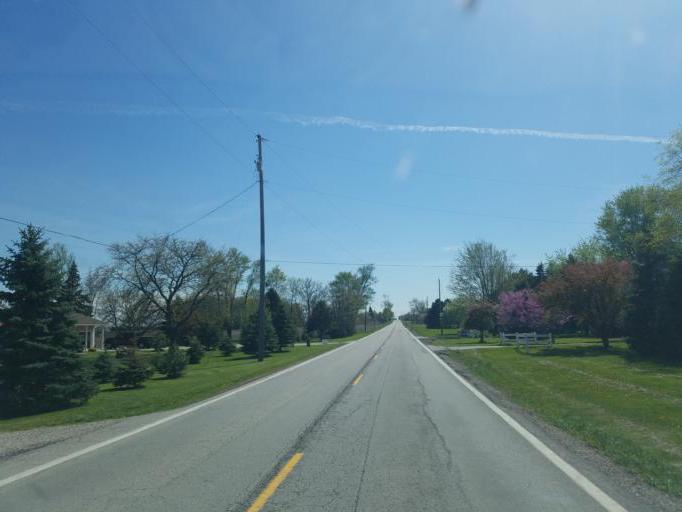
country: US
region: Ohio
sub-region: Huron County
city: Bellevue
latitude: 41.2727
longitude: -82.7914
